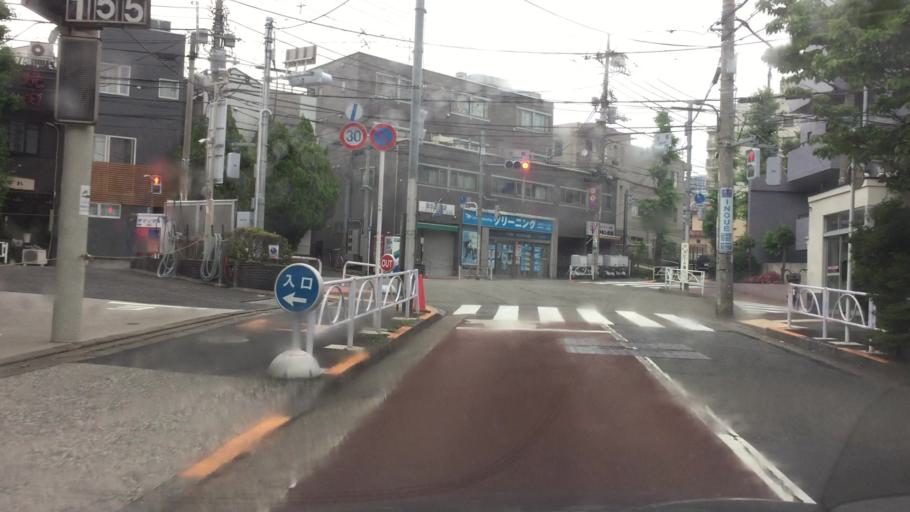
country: JP
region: Tokyo
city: Tokyo
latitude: 35.6411
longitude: 139.6865
